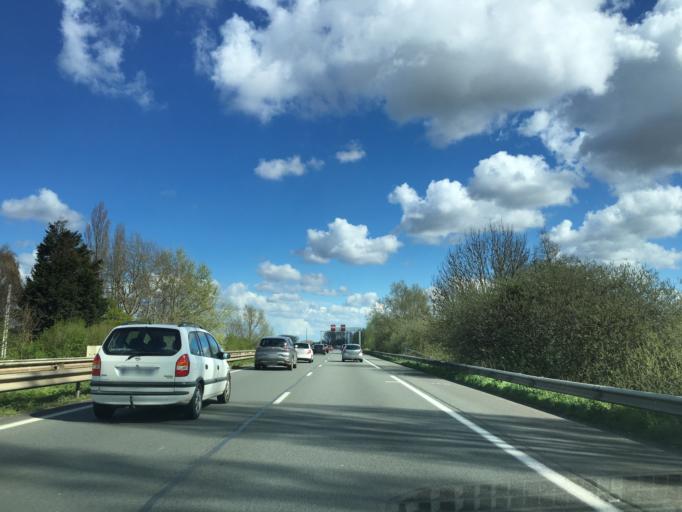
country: FR
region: Nord-Pas-de-Calais
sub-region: Departement du Nord
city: Armentieres
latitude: 50.6722
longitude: 2.8689
